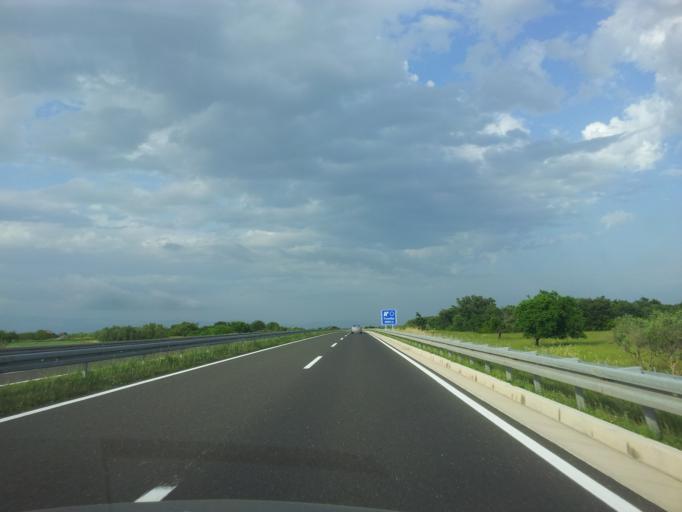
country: HR
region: Zadarska
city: Galovac
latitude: 44.0978
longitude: 15.3801
